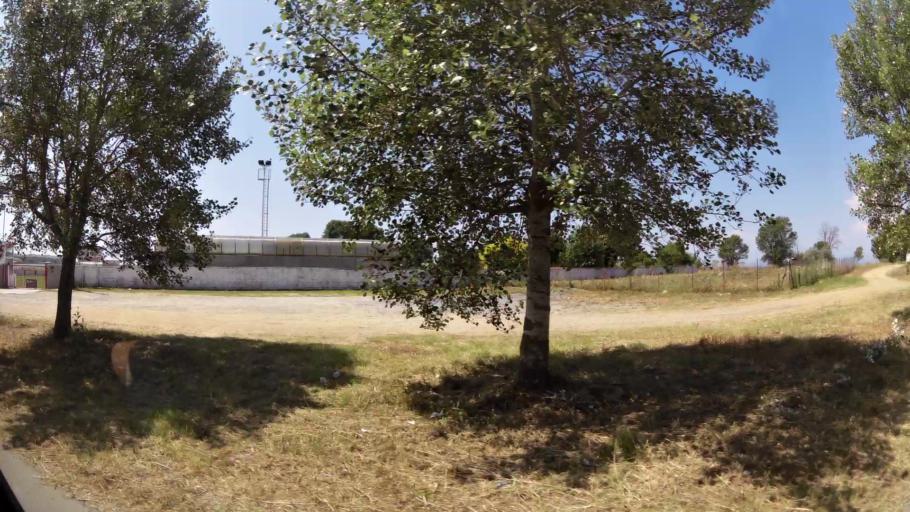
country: GR
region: Central Macedonia
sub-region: Nomos Thessalonikis
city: Nea Michaniona
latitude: 40.4952
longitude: 22.8205
